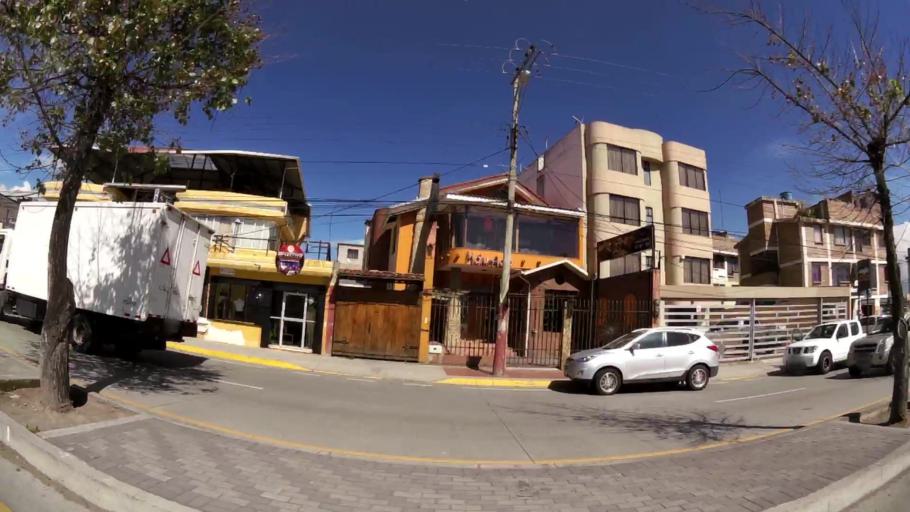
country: EC
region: Chimborazo
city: Riobamba
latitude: -1.6581
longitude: -78.6606
